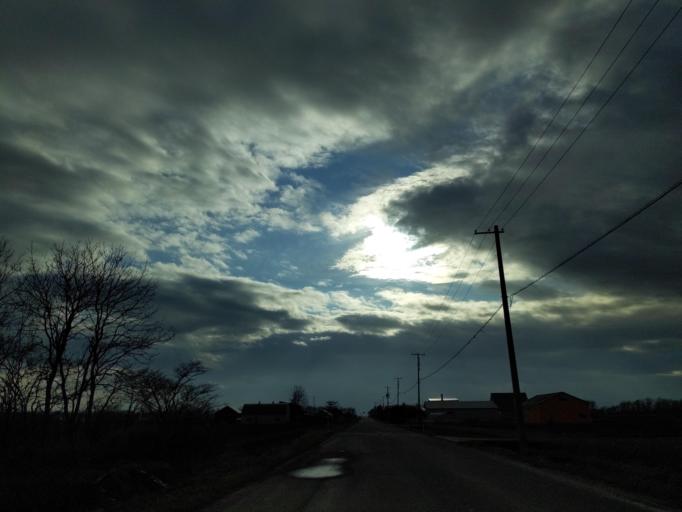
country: JP
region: Hokkaido
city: Kitahiroshima
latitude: 42.9809
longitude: 141.6496
